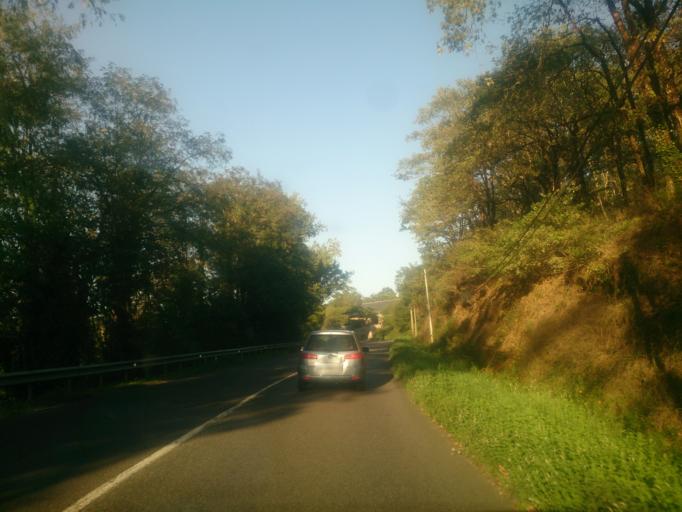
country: FR
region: Limousin
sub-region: Departement de la Correze
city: Brive-la-Gaillarde
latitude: 45.1404
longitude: 1.5192
